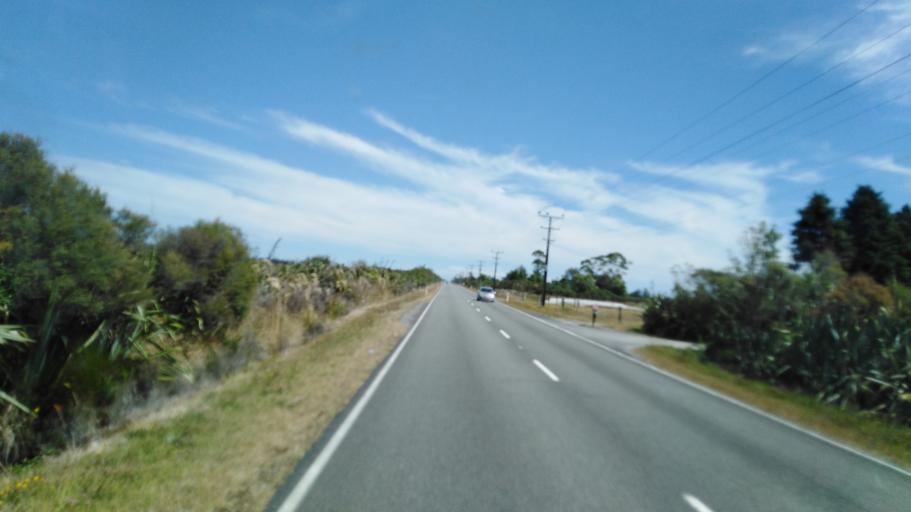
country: NZ
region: West Coast
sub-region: Buller District
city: Westport
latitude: -41.7468
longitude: 171.6820
